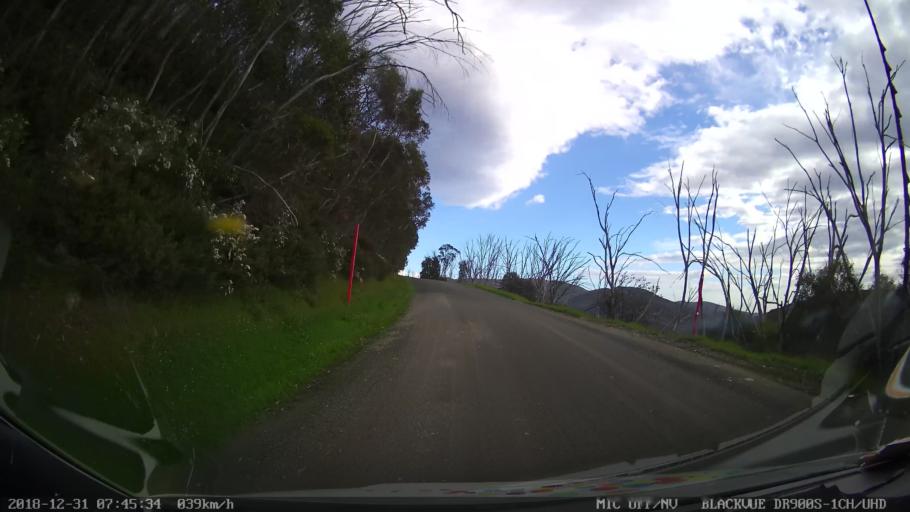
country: AU
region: New South Wales
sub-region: Snowy River
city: Jindabyne
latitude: -36.3634
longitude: 148.4034
